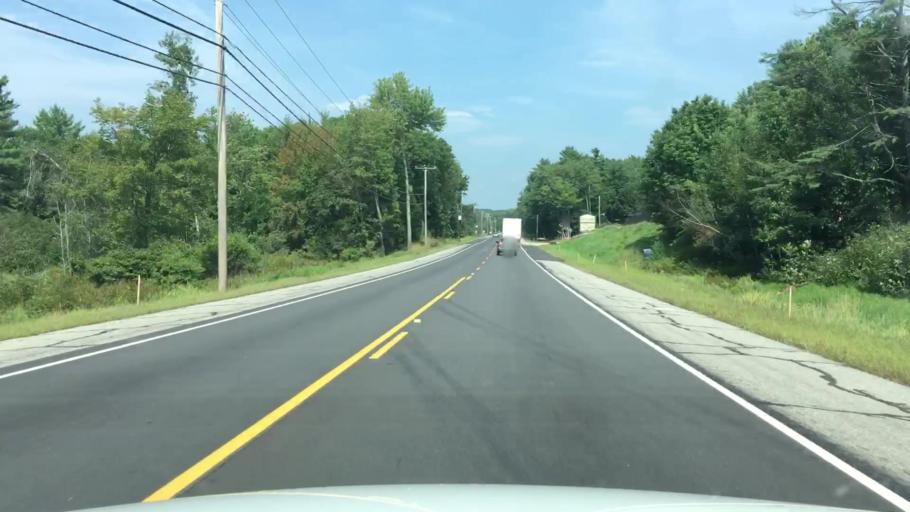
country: US
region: Maine
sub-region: Androscoggin County
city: Turner
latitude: 44.2087
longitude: -70.2459
